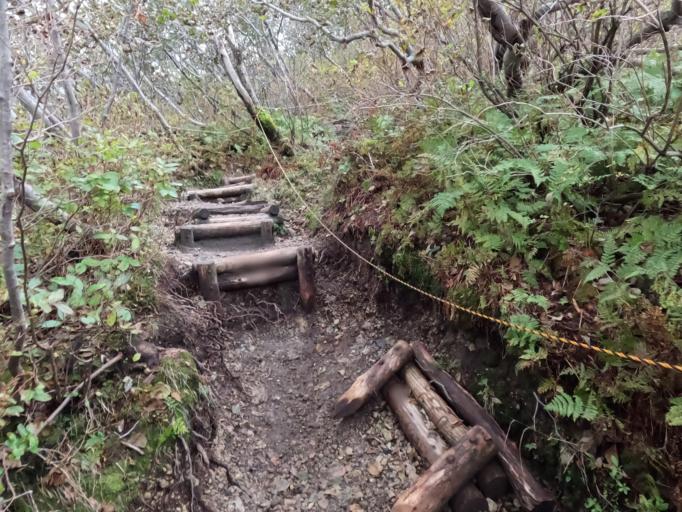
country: JP
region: Hokkaido
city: Shiraoi
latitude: 42.6969
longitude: 141.3908
